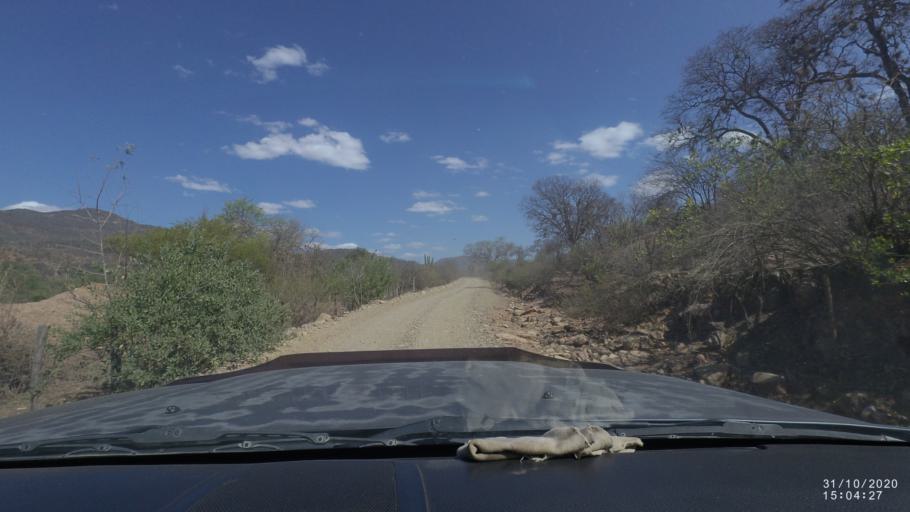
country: BO
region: Cochabamba
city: Aiquile
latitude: -18.2827
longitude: -64.8032
